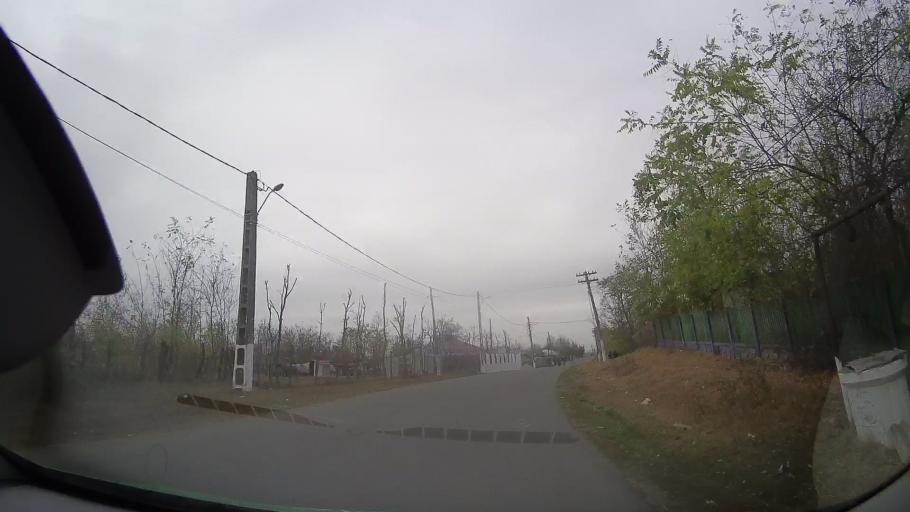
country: RO
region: Braila
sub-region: Comuna Ulmu
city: Jugureanu
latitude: 44.9432
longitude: 27.2689
